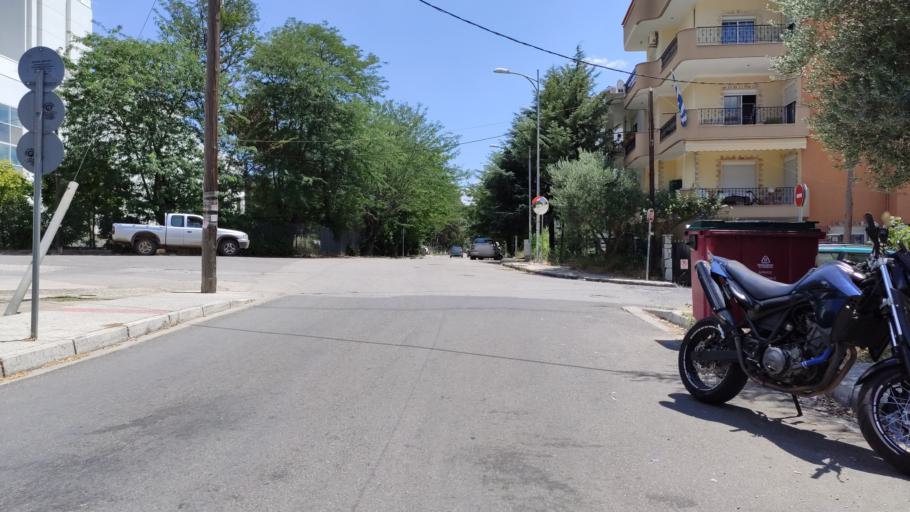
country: GR
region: East Macedonia and Thrace
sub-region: Nomos Rodopis
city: Komotini
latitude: 41.1289
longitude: 25.4097
